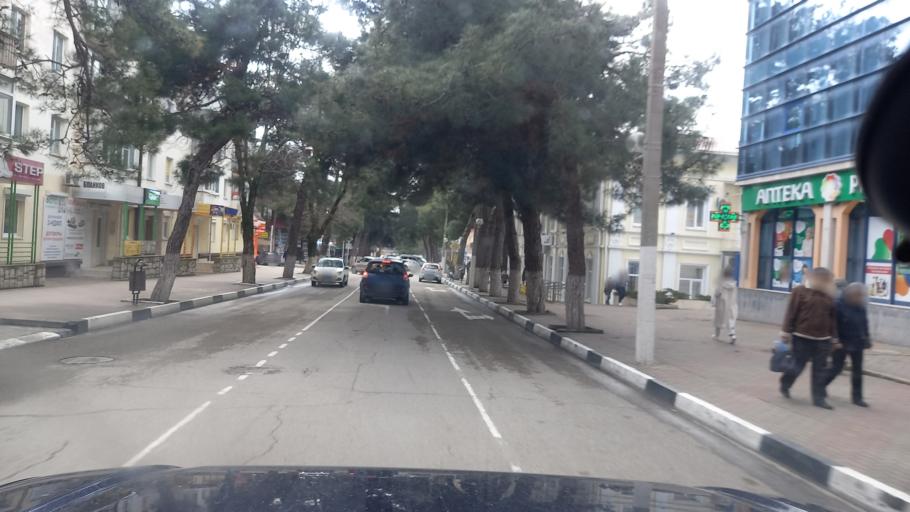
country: RU
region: Krasnodarskiy
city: Gelendzhik
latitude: 44.5631
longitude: 38.0814
